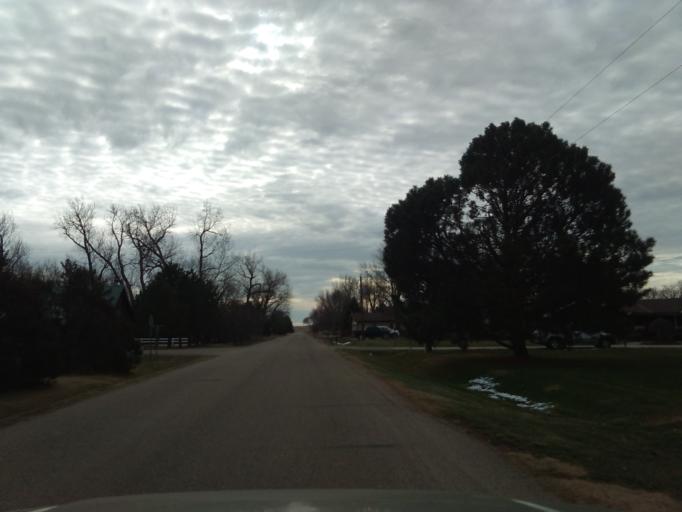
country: US
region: Nebraska
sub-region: Hall County
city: Grand Island
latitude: 40.7767
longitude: -98.4120
